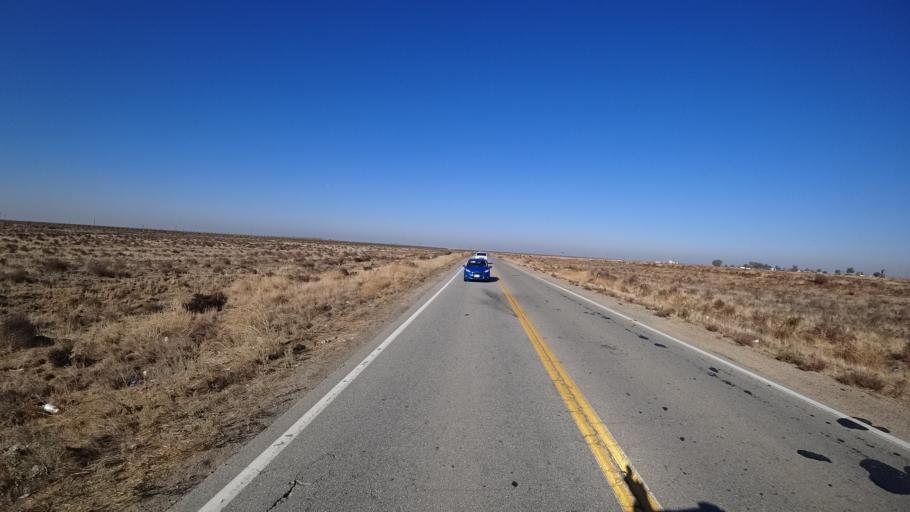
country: US
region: California
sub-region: Kern County
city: Rosedale
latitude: 35.4294
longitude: -119.1472
